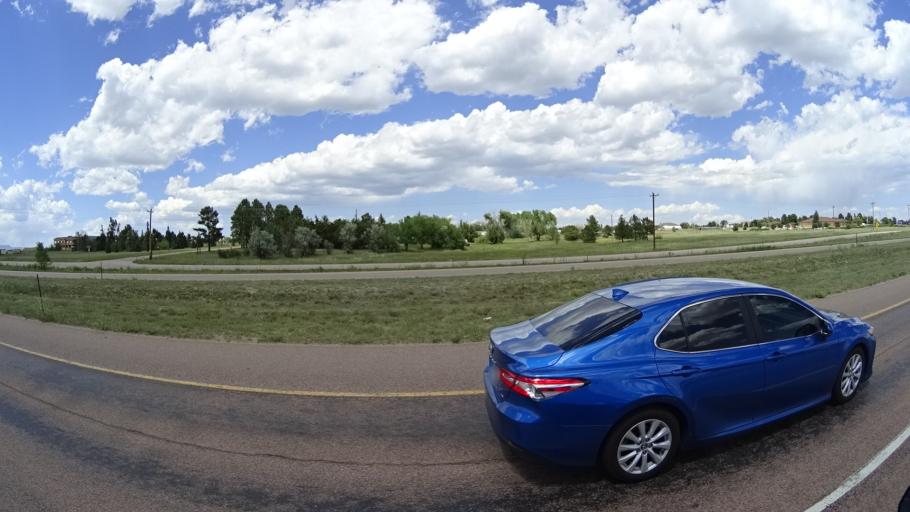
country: US
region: Colorado
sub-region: El Paso County
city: Black Forest
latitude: 38.9405
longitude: -104.6699
